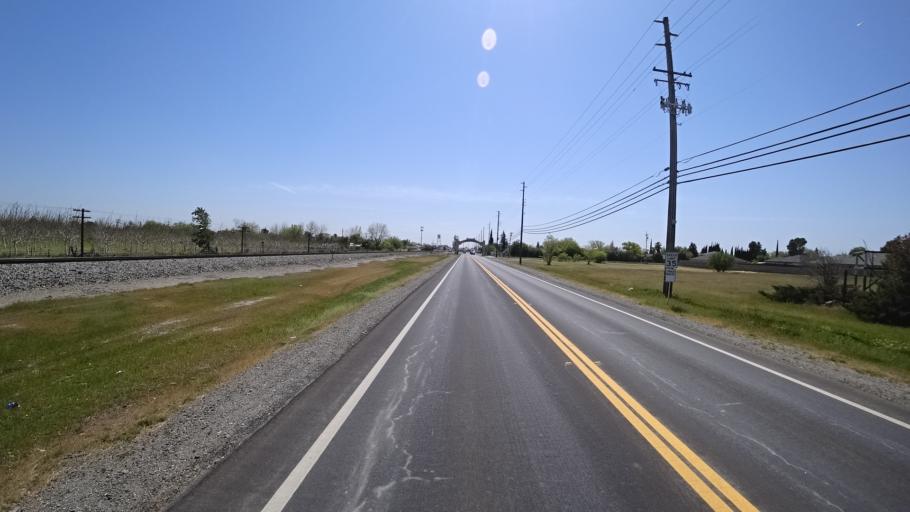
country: US
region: California
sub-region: Glenn County
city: Orland
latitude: 39.7559
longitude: -122.1970
